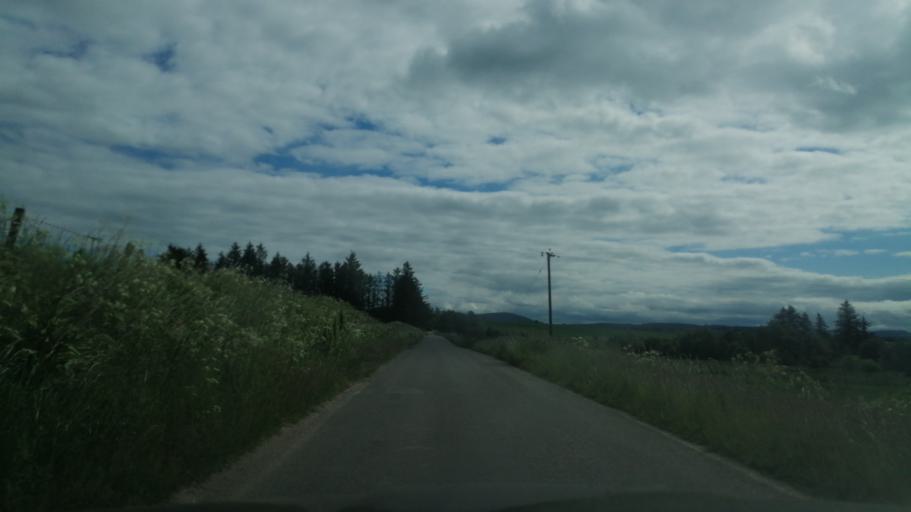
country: GB
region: Scotland
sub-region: Moray
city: Keith
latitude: 57.5560
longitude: -2.9456
